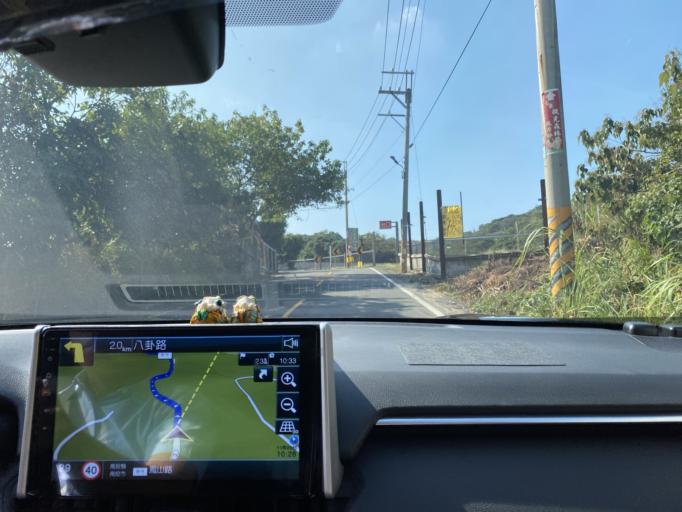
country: TW
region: Taiwan
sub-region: Nantou
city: Nantou
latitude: 23.9439
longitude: 120.6518
